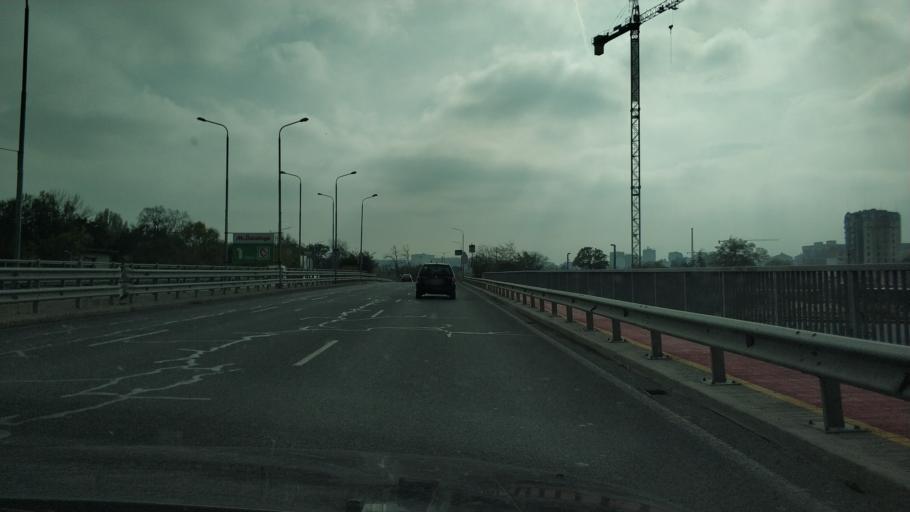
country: BG
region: Plovdiv
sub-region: Obshtina Plovdiv
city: Plovdiv
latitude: 42.1547
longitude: 24.7657
